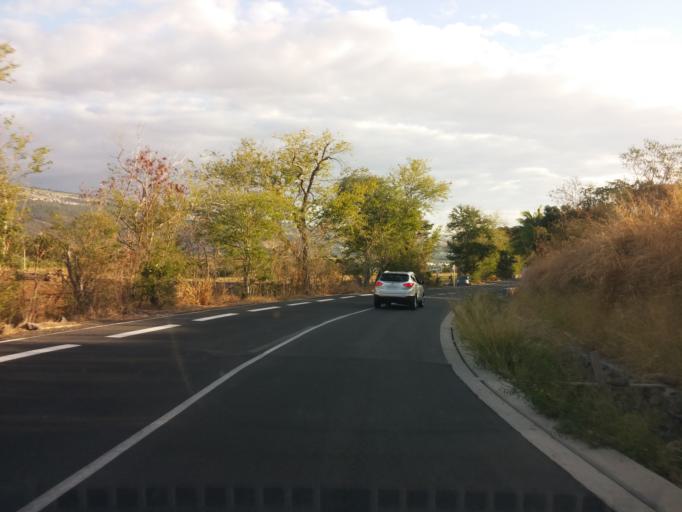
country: RE
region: Reunion
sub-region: Reunion
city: Le Port
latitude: -20.9713
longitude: 55.3088
